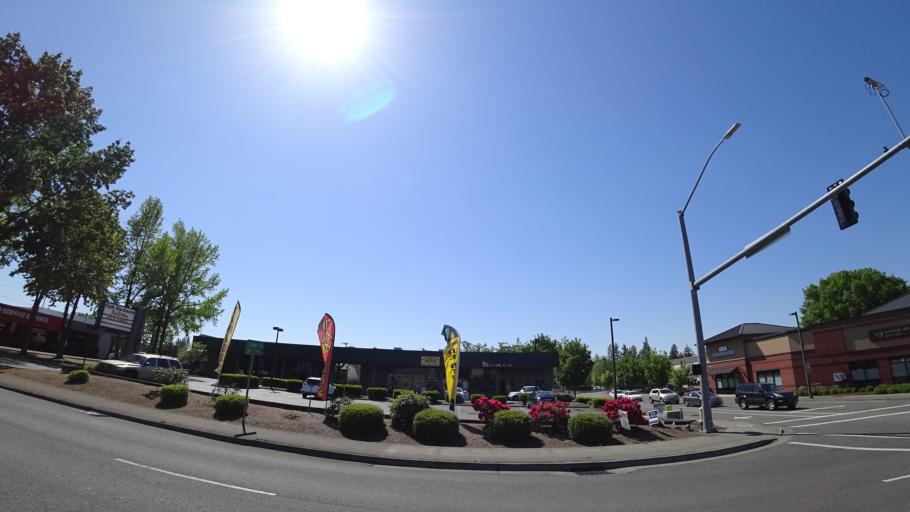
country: US
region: Oregon
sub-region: Washington County
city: Beaverton
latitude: 45.4894
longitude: -122.8108
